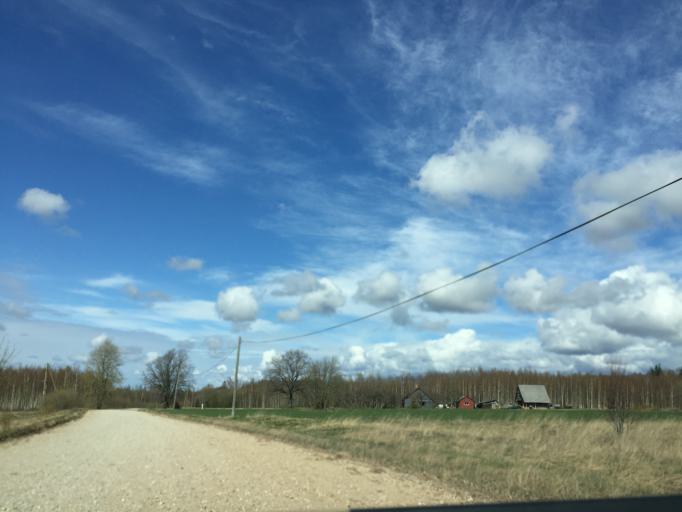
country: LV
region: Limbazu Rajons
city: Limbazi
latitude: 57.5744
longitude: 24.5949
